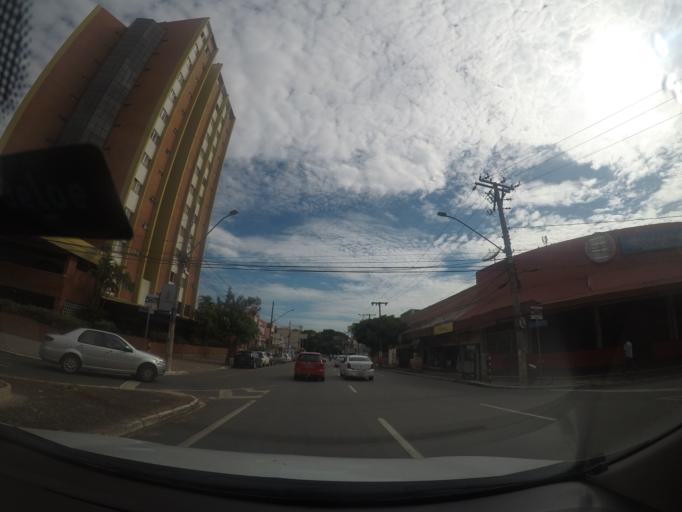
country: BR
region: Goias
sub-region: Goiania
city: Goiania
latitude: -16.6724
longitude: -49.2544
